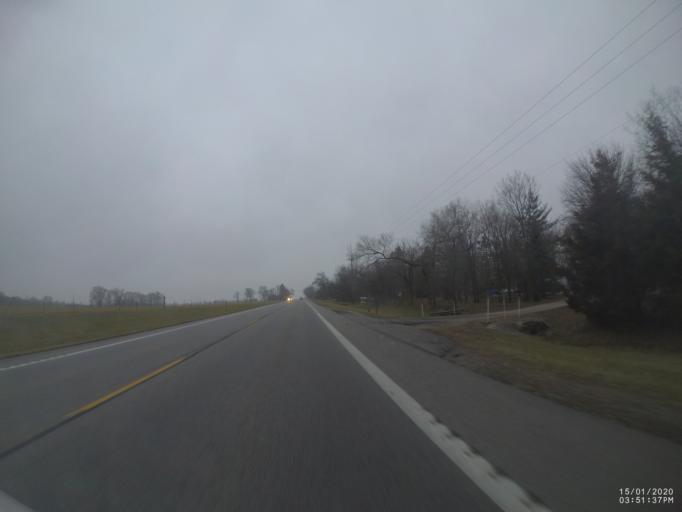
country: US
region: Ohio
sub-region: Wood County
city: Pemberville
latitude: 41.4170
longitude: -83.4160
